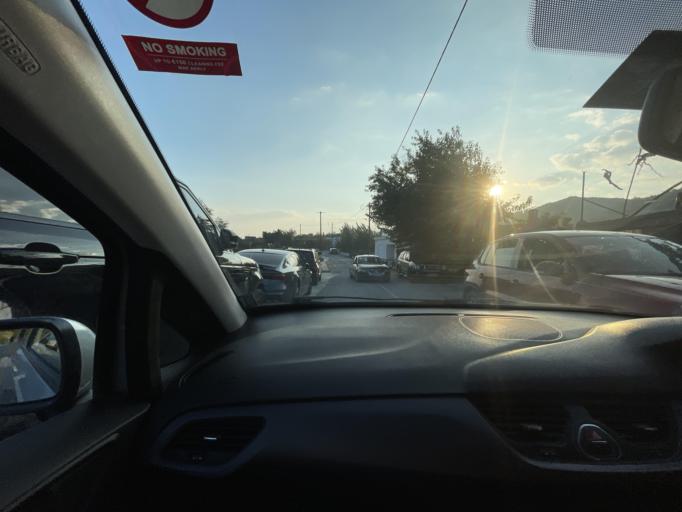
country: CY
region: Limassol
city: Pelendri
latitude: 34.8923
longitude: 32.9656
